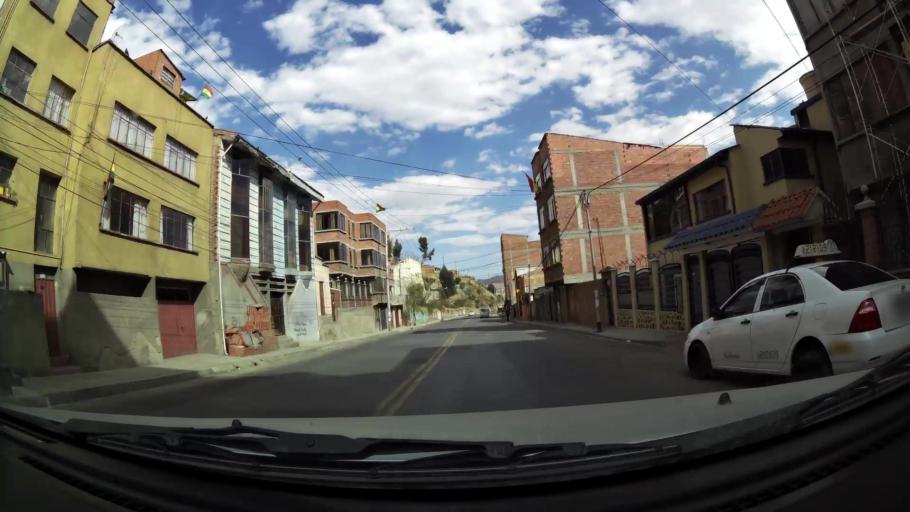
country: BO
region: La Paz
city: La Paz
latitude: -16.4702
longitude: -68.1516
